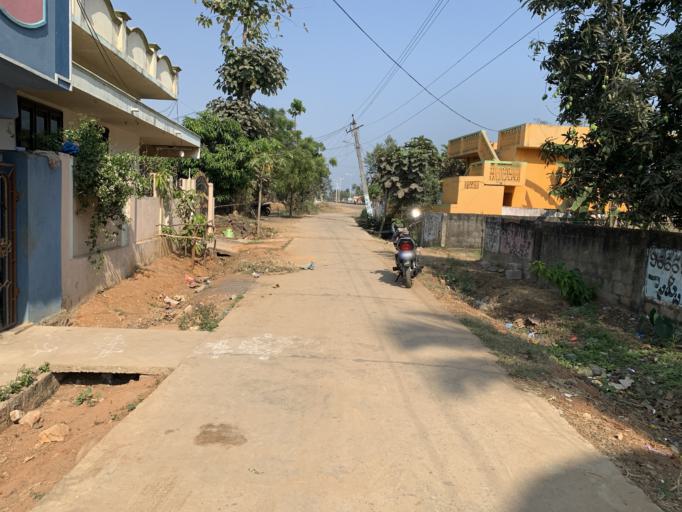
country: IN
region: Andhra Pradesh
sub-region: East Godavari
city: Peddapuram
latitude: 17.1636
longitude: 82.0251
